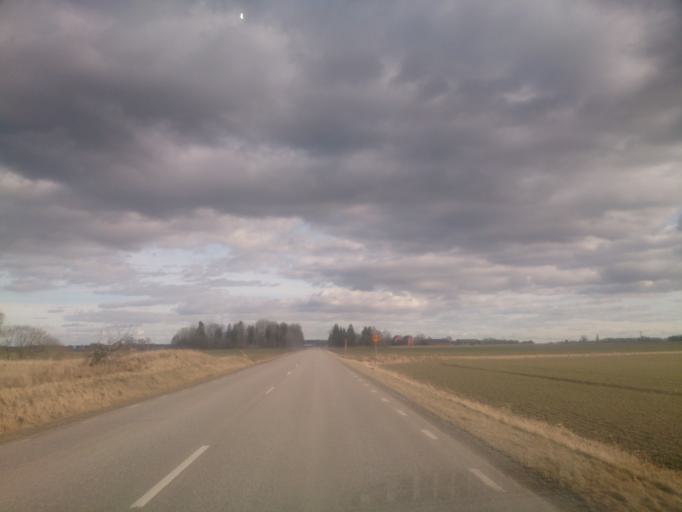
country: SE
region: OEstergoetland
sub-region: Motala Kommun
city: Stenstorp
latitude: 58.5172
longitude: 15.1768
